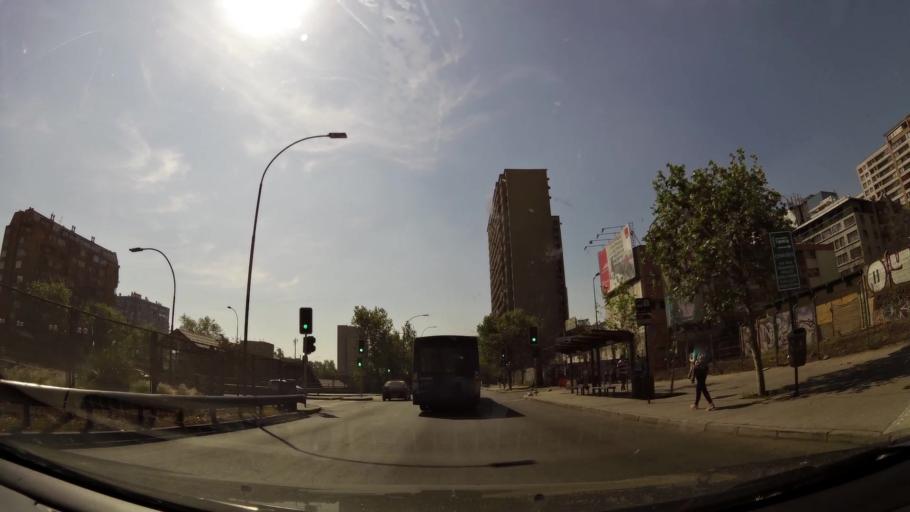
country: CL
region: Santiago Metropolitan
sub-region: Provincia de Santiago
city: Santiago
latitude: -33.4396
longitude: -70.6594
